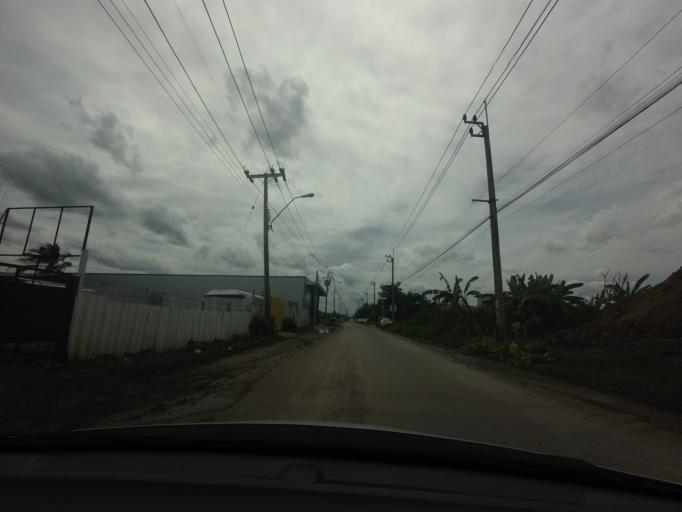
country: TH
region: Bangkok
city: Min Buri
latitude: 13.7911
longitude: 100.7589
